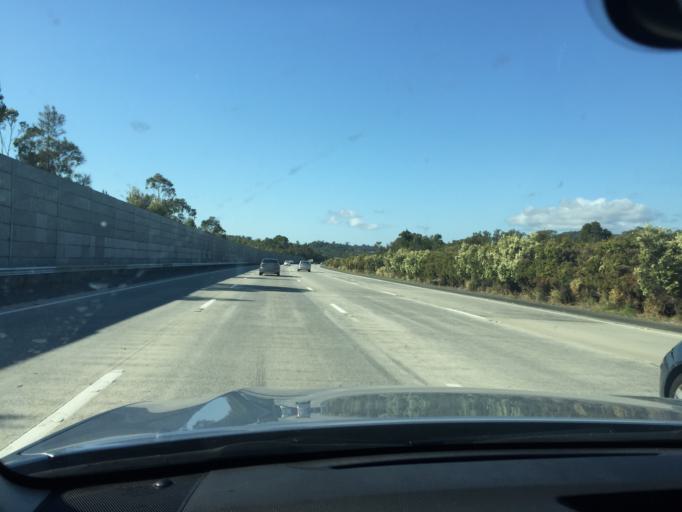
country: AU
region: Queensland
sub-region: Gold Coast
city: Ormeau Hills
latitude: -27.7902
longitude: 153.2589
